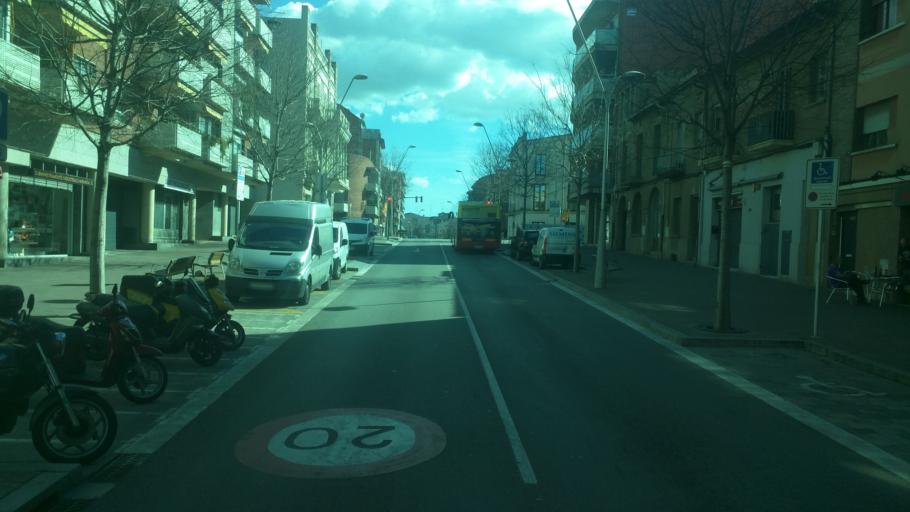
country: ES
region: Catalonia
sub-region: Provincia de Barcelona
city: Sant Feliu de Llobregat
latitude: 41.3846
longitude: 2.0411
